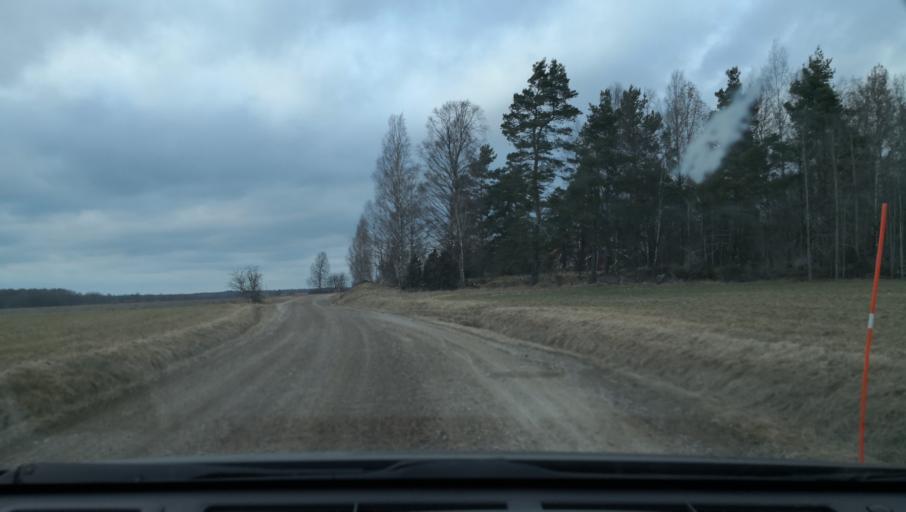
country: SE
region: Vaestmanland
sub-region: Kopings Kommun
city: Koping
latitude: 59.5205
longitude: 15.9137
